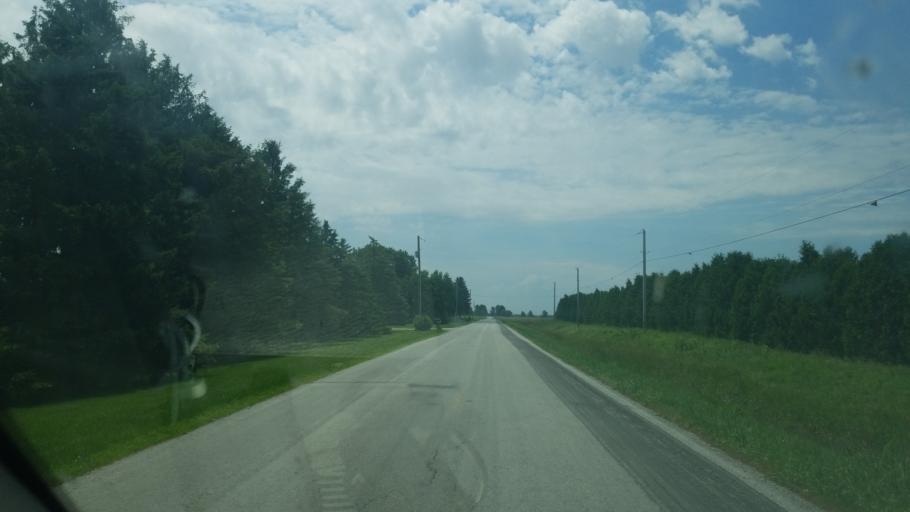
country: US
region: Ohio
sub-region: Wood County
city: North Baltimore
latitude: 41.2630
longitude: -83.5929
